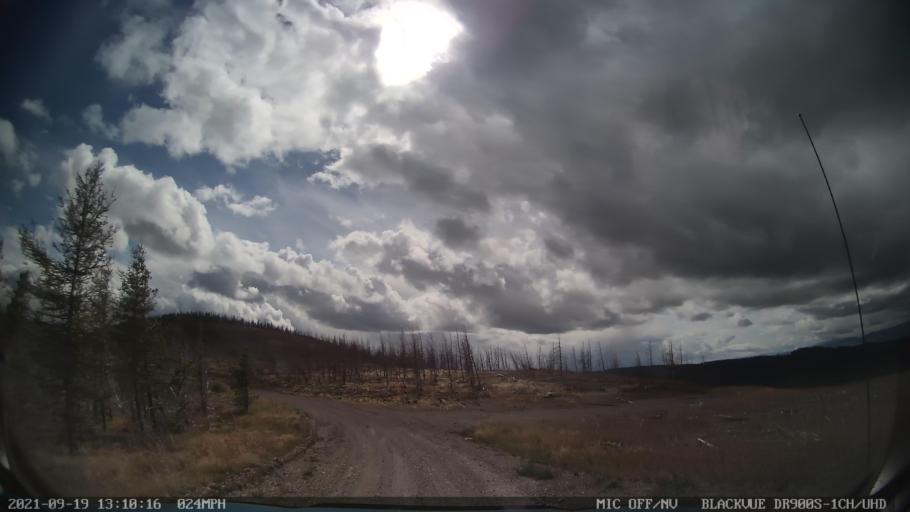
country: US
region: Montana
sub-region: Missoula County
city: Seeley Lake
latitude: 47.1789
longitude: -113.3530
